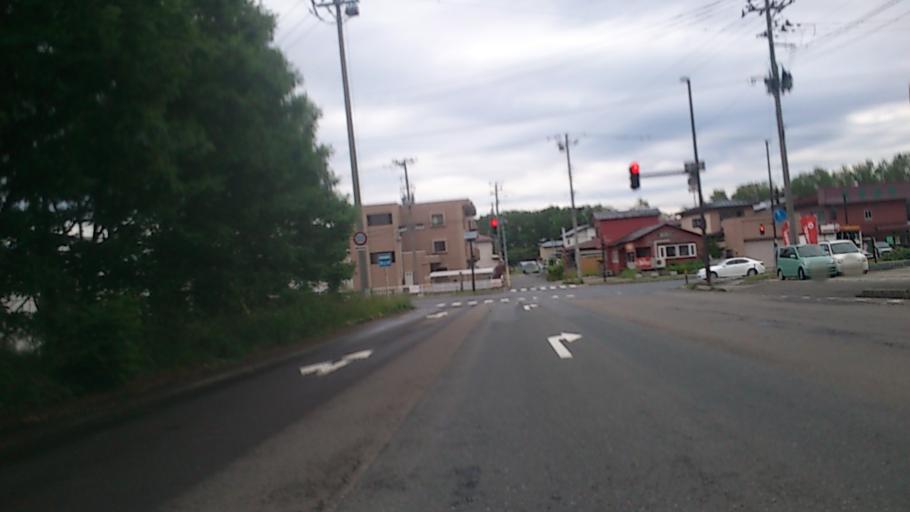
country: JP
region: Akita
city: Noshiromachi
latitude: 40.1876
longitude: 140.0119
